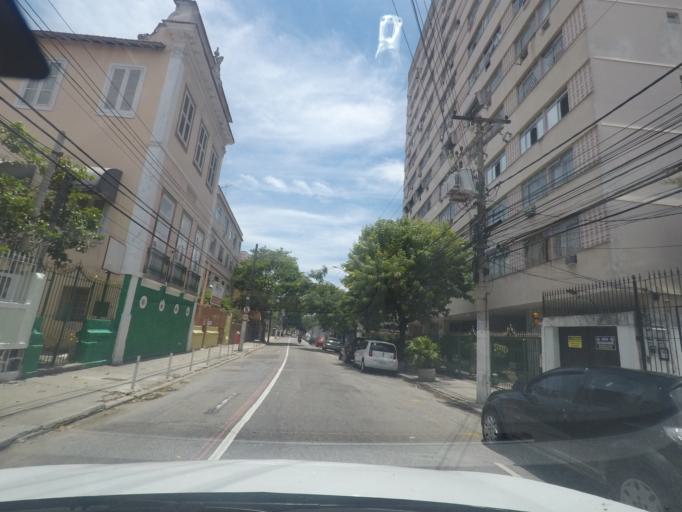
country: BR
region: Rio de Janeiro
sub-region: Niteroi
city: Niteroi
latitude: -22.9001
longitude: -43.1287
